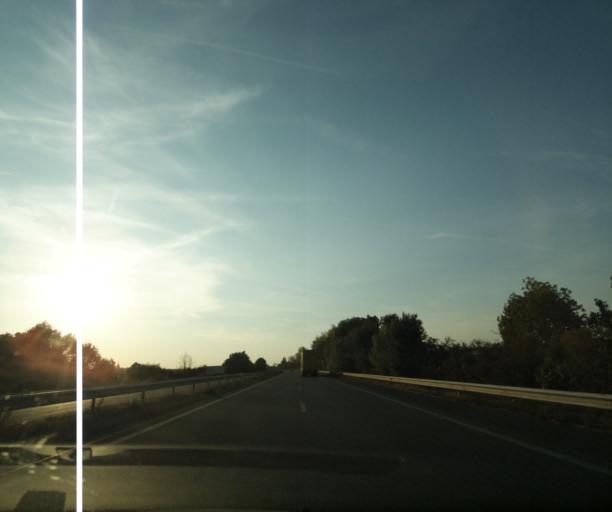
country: FR
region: Midi-Pyrenees
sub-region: Departement du Tarn-et-Garonne
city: Saint-Nicolas-de-la-Grave
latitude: 44.0489
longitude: 0.9836
